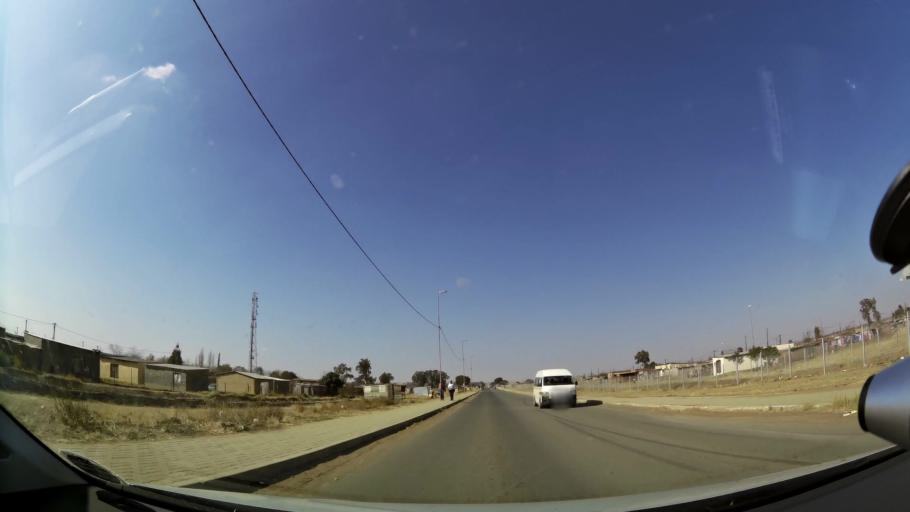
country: ZA
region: Orange Free State
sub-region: Mangaung Metropolitan Municipality
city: Bloemfontein
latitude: -29.1686
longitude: 26.2901
